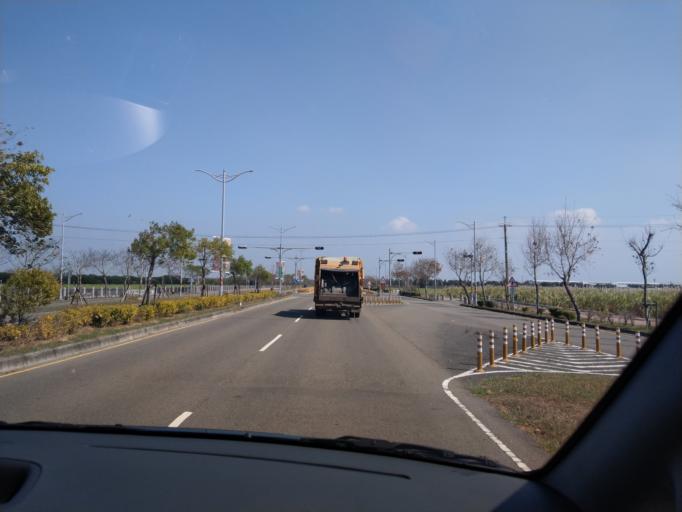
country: TW
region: Taiwan
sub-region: Chiayi
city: Taibao
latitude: 23.4670
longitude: 120.3125
